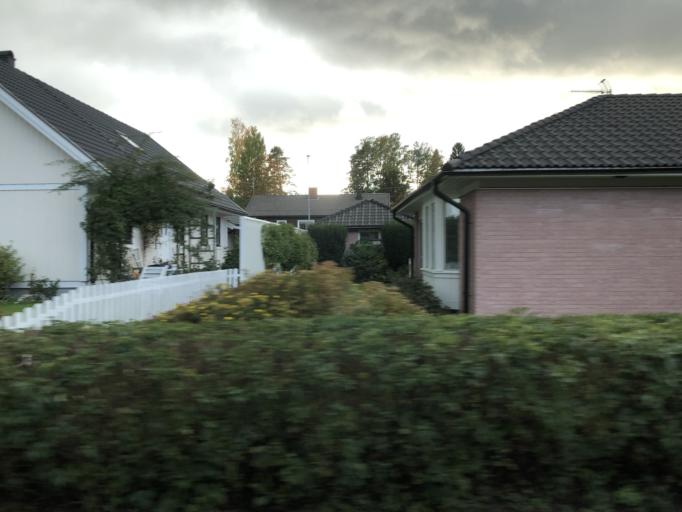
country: SE
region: Stockholm
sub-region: Jarfalla Kommun
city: Jakobsberg
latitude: 59.4276
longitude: 17.8219
